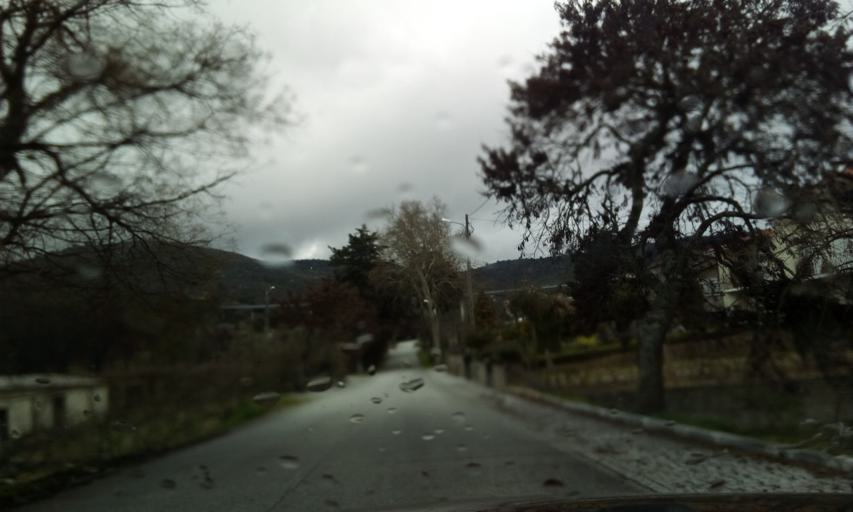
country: PT
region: Guarda
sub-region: Fornos de Algodres
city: Fornos de Algodres
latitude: 40.6198
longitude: -7.5867
